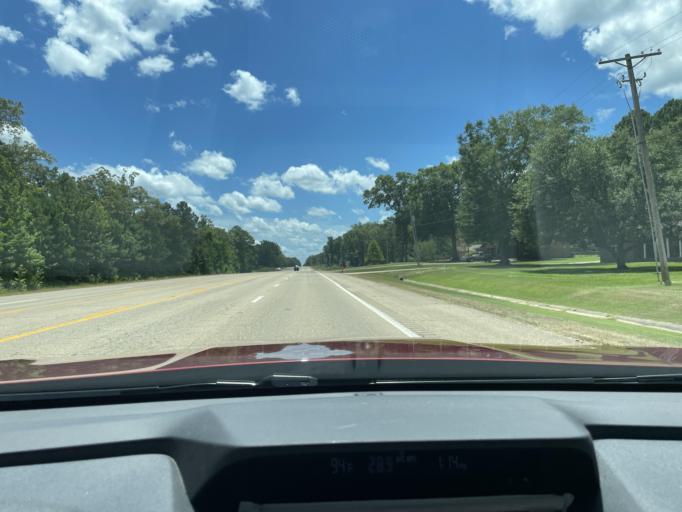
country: US
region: Arkansas
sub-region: Drew County
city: Monticello
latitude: 33.6665
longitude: -91.8038
